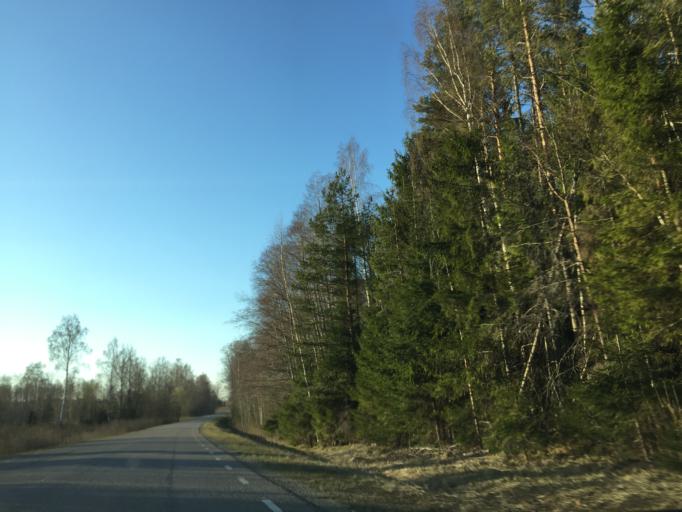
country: EE
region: Ida-Virumaa
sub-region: Toila vald
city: Voka
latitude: 59.1775
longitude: 27.5672
